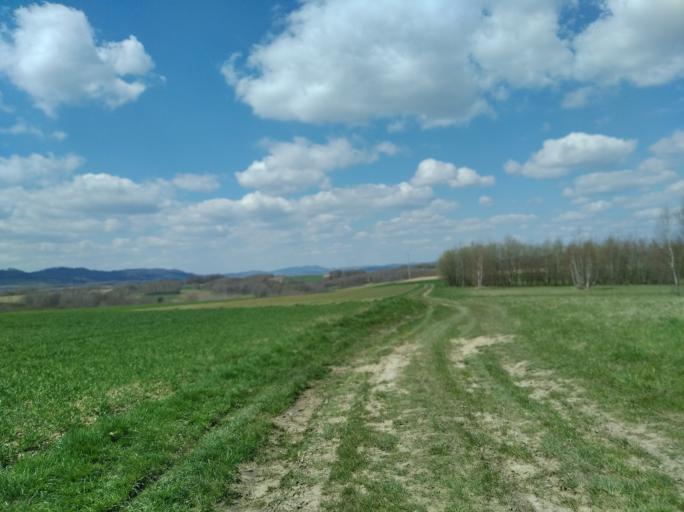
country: PL
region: Subcarpathian Voivodeship
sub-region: Powiat strzyzowski
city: Wysoka Strzyzowska
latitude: 49.8426
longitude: 21.7595
